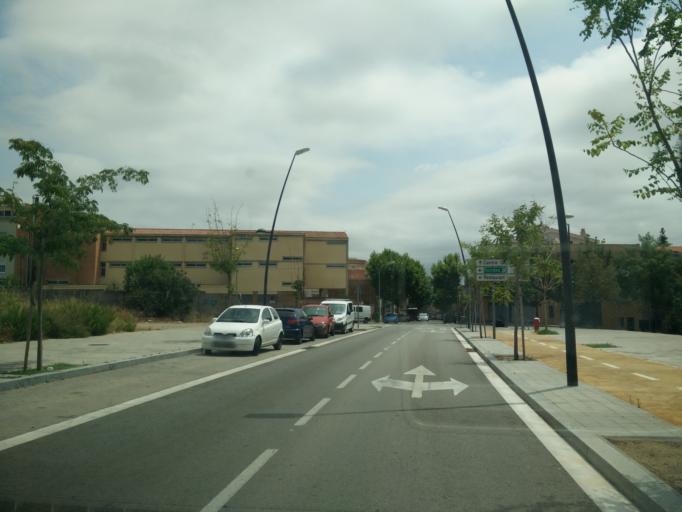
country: ES
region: Catalonia
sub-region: Provincia de Barcelona
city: Terrassa
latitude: 41.5798
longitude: 2.0021
